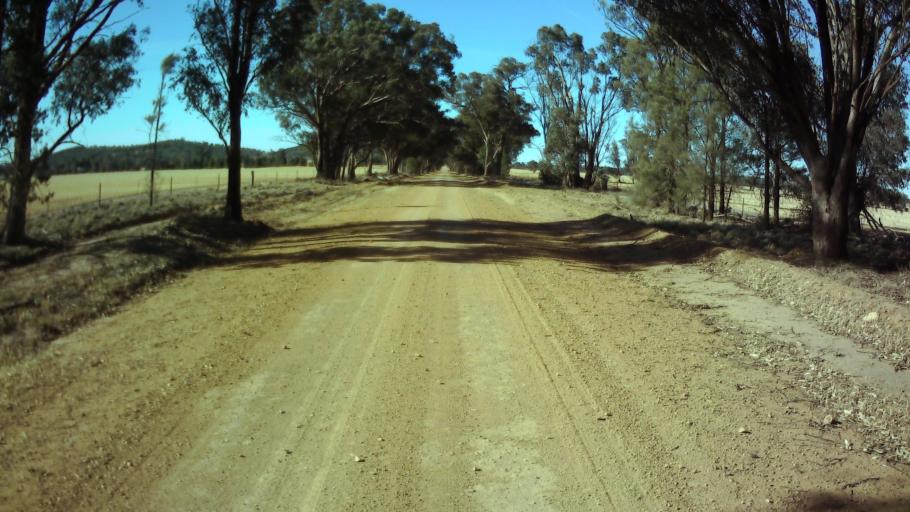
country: AU
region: New South Wales
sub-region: Weddin
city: Grenfell
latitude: -33.8139
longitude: 147.8767
